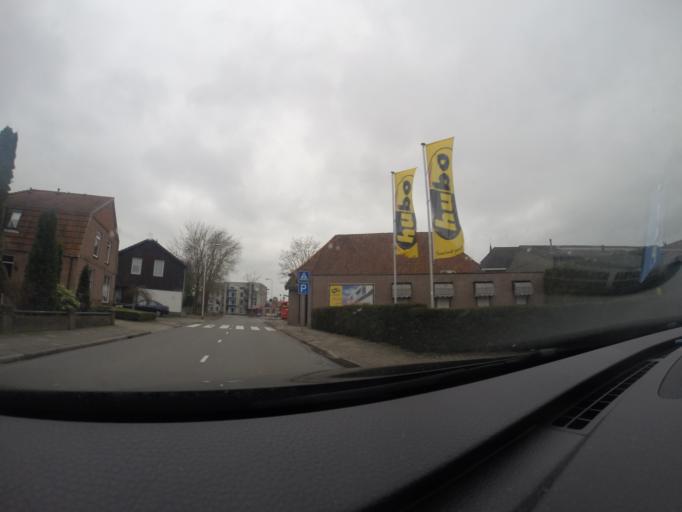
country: NL
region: Overijssel
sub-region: Gemeente Haaksbergen
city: Haaksbergen
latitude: 52.1534
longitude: 6.7447
